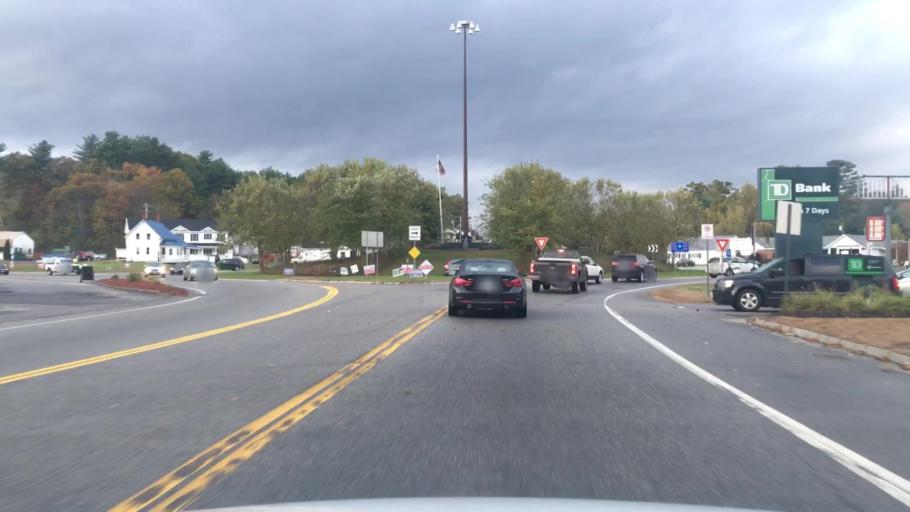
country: US
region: New Hampshire
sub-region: Merrimack County
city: Epsom
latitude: 43.2276
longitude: -71.3594
